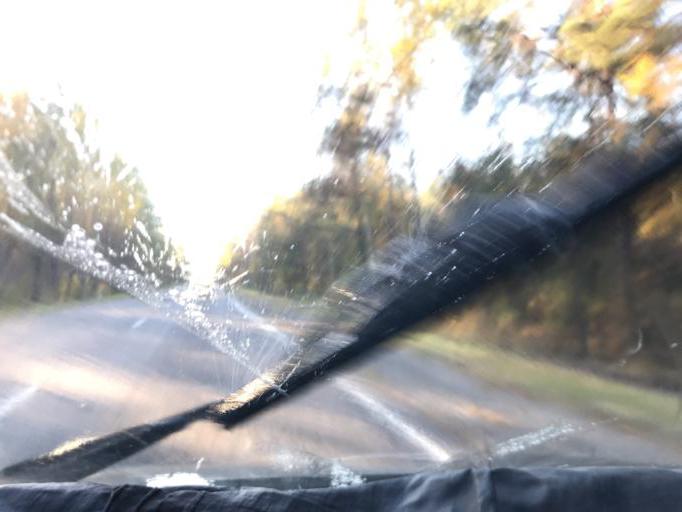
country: BY
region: Gomel
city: Pyetrykaw
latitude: 52.2748
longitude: 28.2345
